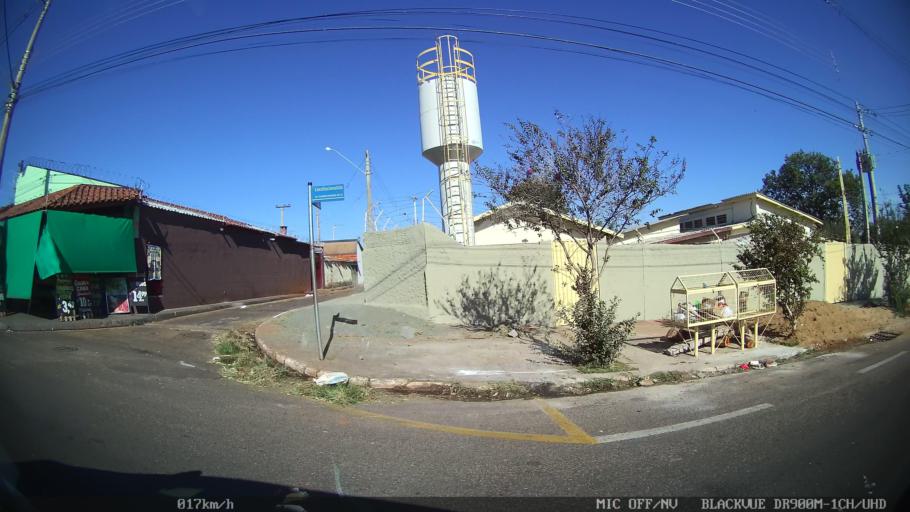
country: BR
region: Sao Paulo
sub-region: Olimpia
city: Olimpia
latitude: -20.7263
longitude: -48.9118
